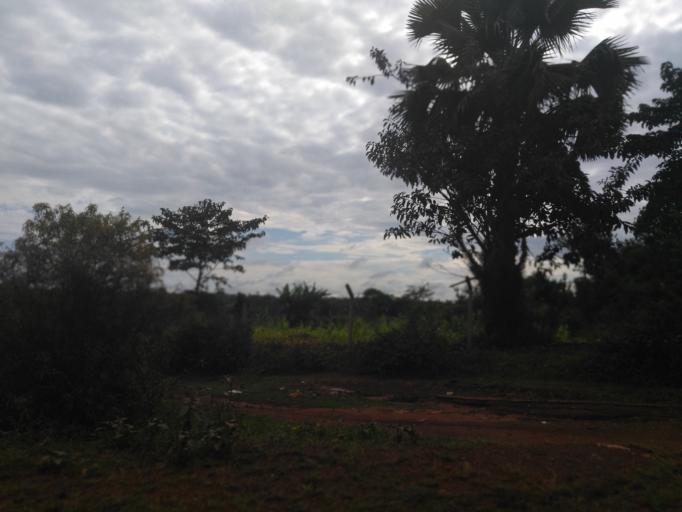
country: UG
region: Eastern Region
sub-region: Jinja District
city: Jinja
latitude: 0.4278
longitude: 33.1910
